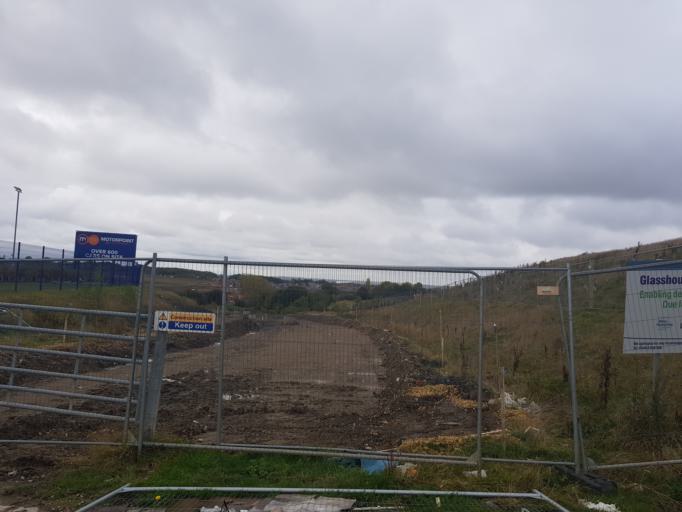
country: GB
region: England
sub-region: City and Borough of Wakefield
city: Castleford
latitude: 53.7076
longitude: -1.3531
